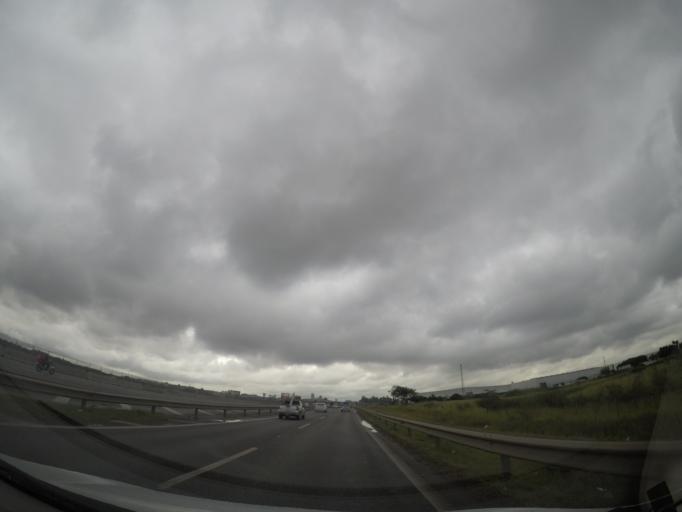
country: BR
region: Sao Paulo
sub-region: Guarulhos
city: Guarulhos
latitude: -23.4790
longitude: -46.4448
